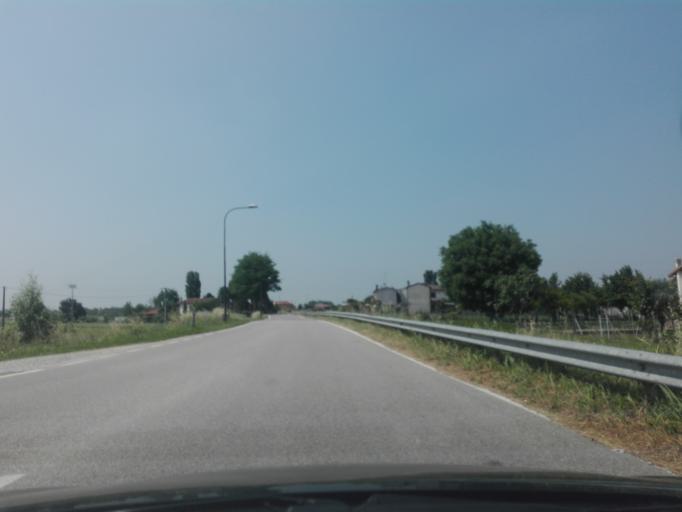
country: IT
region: Veneto
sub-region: Provincia di Rovigo
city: Villadose
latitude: 45.0708
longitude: 11.8821
